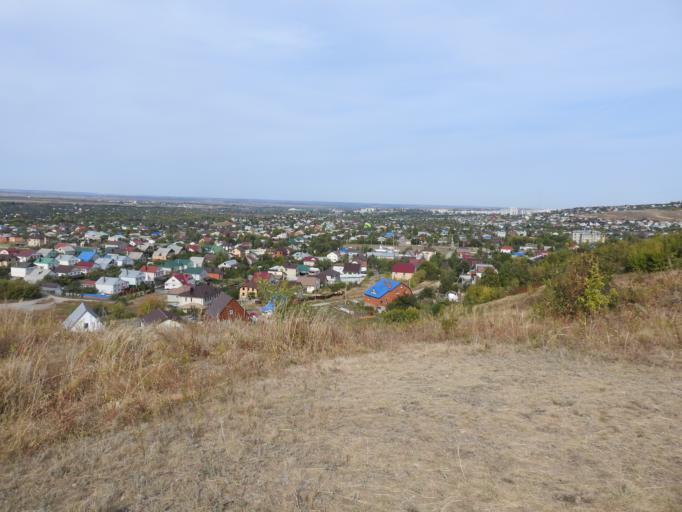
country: RU
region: Saratov
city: Sokolovyy
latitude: 51.5689
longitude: 45.8767
